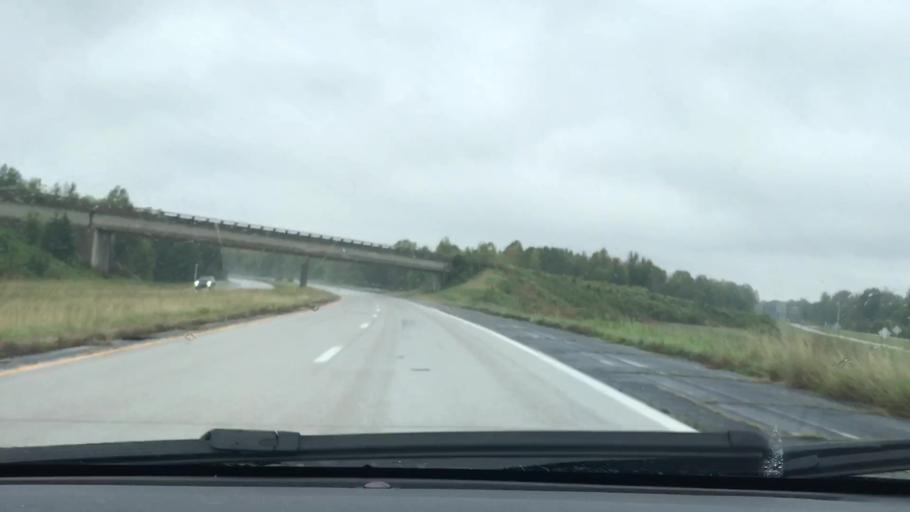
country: US
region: Kentucky
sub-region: Hopkins County
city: Nortonville
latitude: 37.1497
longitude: -87.4650
